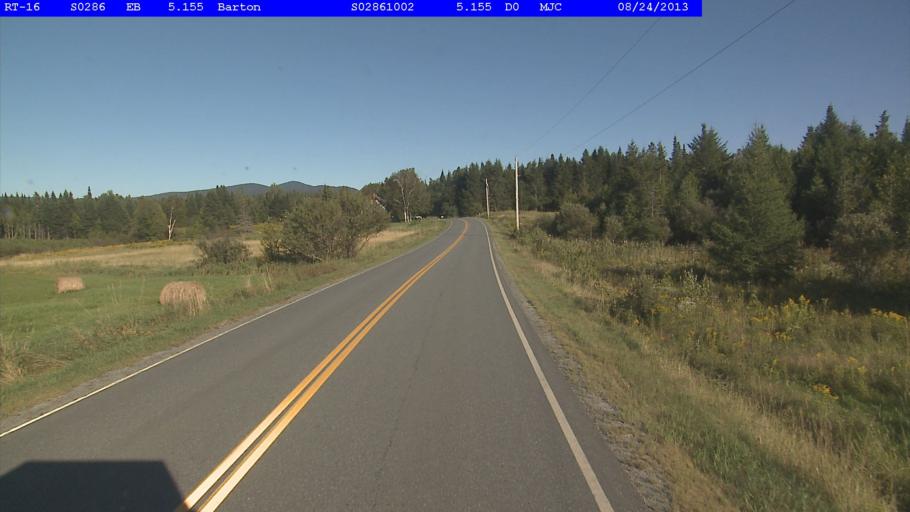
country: US
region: Vermont
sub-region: Orleans County
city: Newport
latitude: 44.7845
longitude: -72.1053
